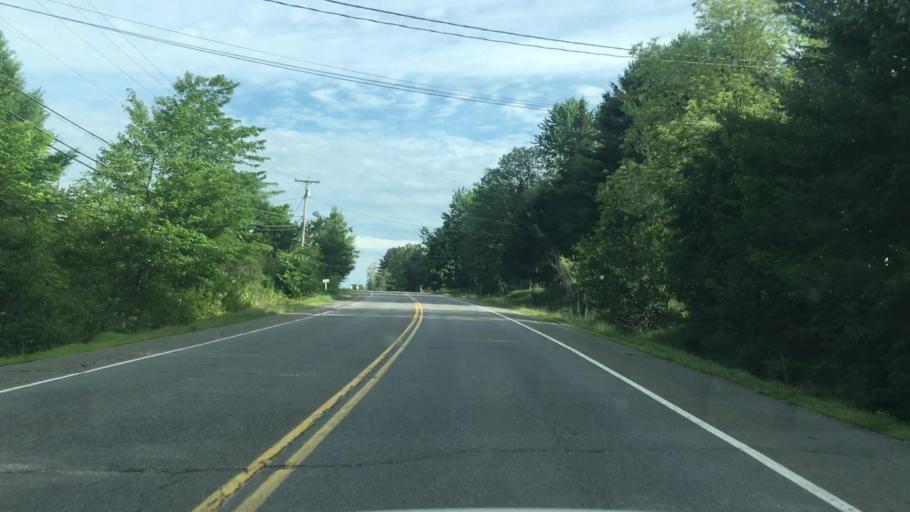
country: US
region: Maine
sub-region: Cumberland County
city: Gorham
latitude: 43.6448
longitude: -70.4221
